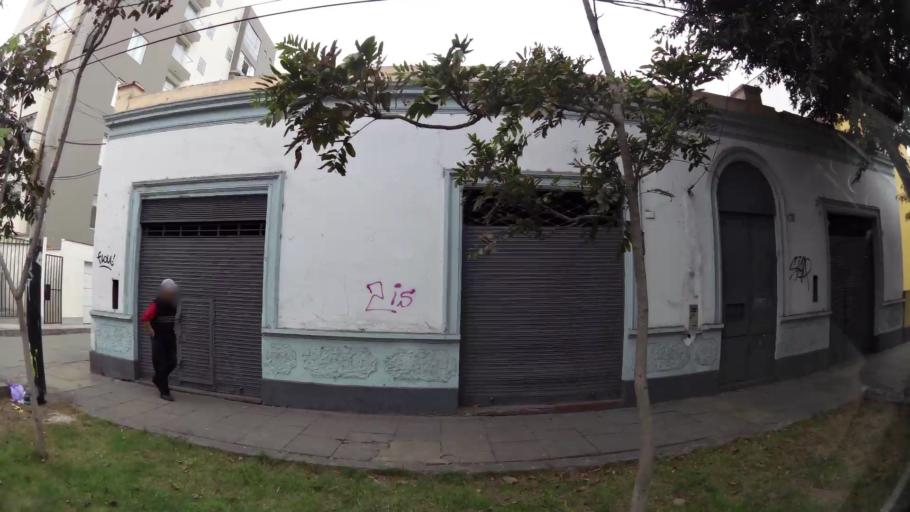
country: PE
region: Lima
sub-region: Lima
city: Surco
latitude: -12.1394
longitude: -77.0203
